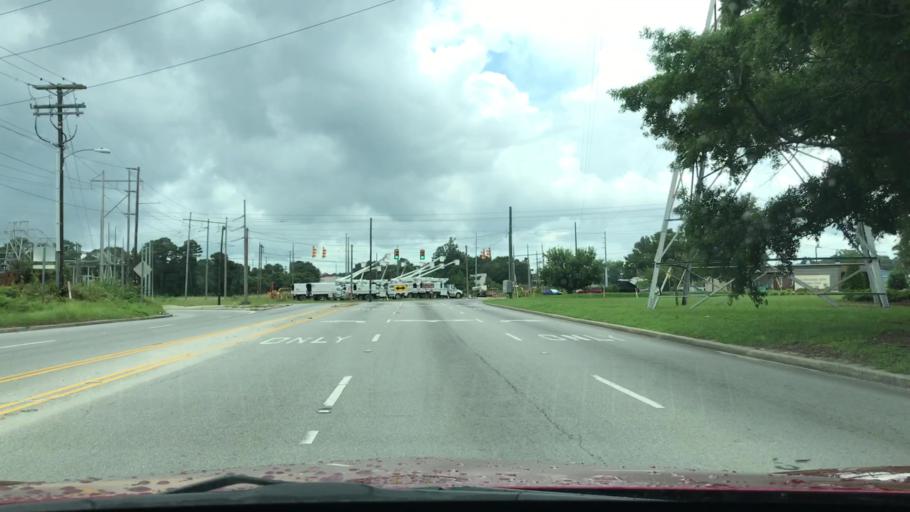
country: US
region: South Carolina
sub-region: Charleston County
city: North Charleston
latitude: 32.8496
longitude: -80.0117
